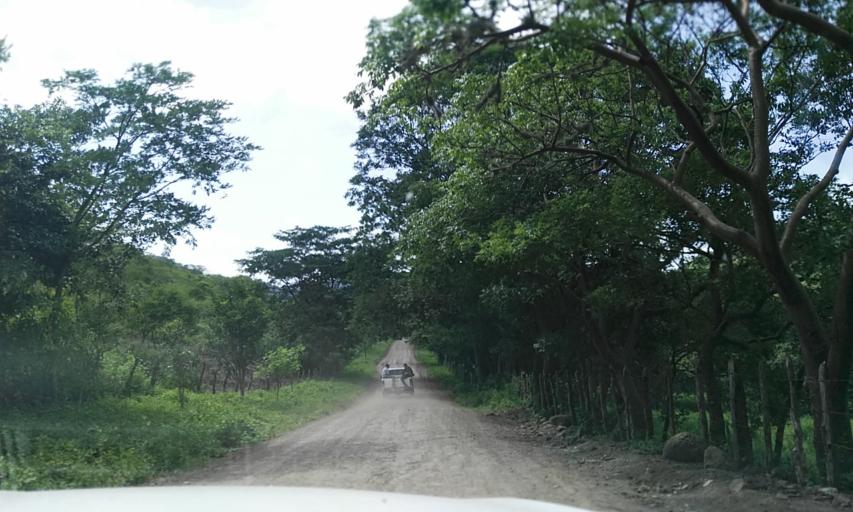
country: NI
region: Matagalpa
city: Terrabona
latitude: 12.7111
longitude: -85.9596
